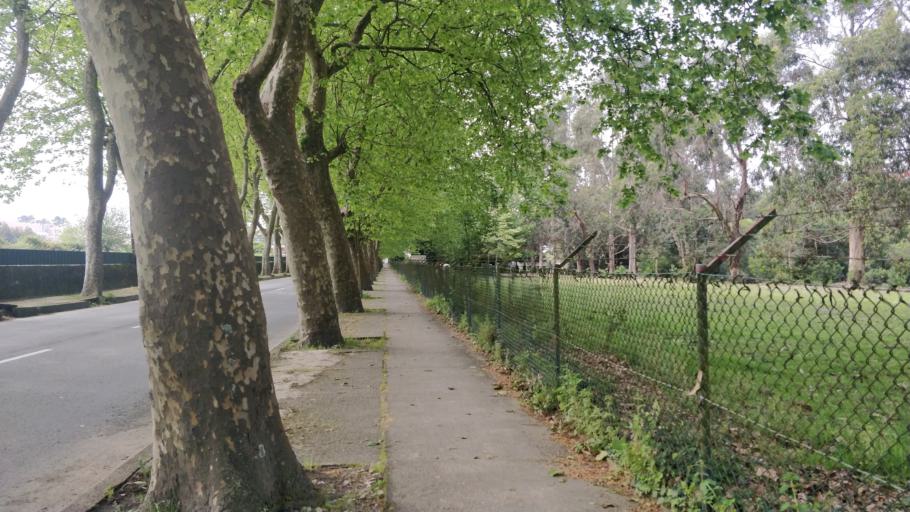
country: PT
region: Viana do Castelo
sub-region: Viana do Castelo
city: Viana do Castelo
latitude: 41.6864
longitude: -8.8153
